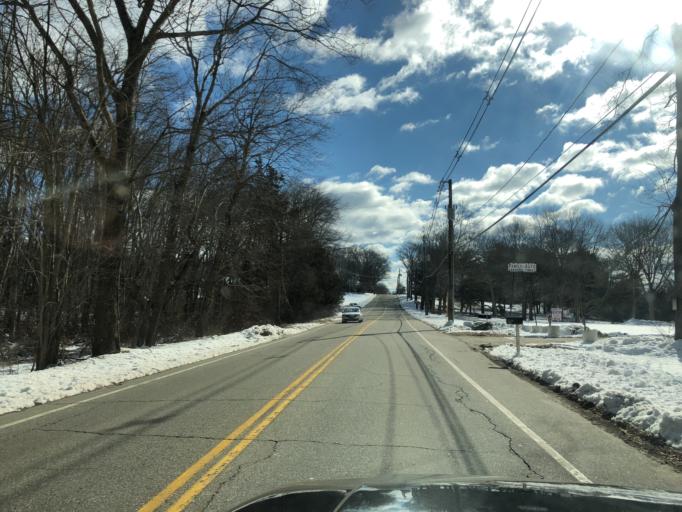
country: US
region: Connecticut
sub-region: New London County
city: Colchester
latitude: 41.5817
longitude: -72.3541
